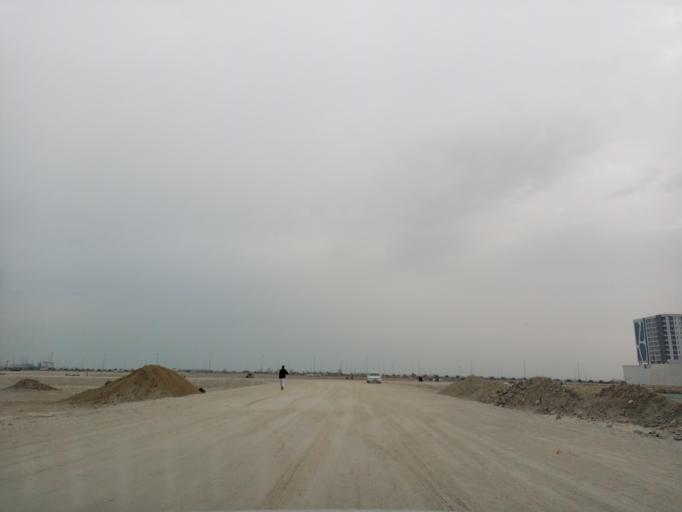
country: BH
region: Muharraq
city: Al Hadd
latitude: 26.2297
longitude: 50.6423
